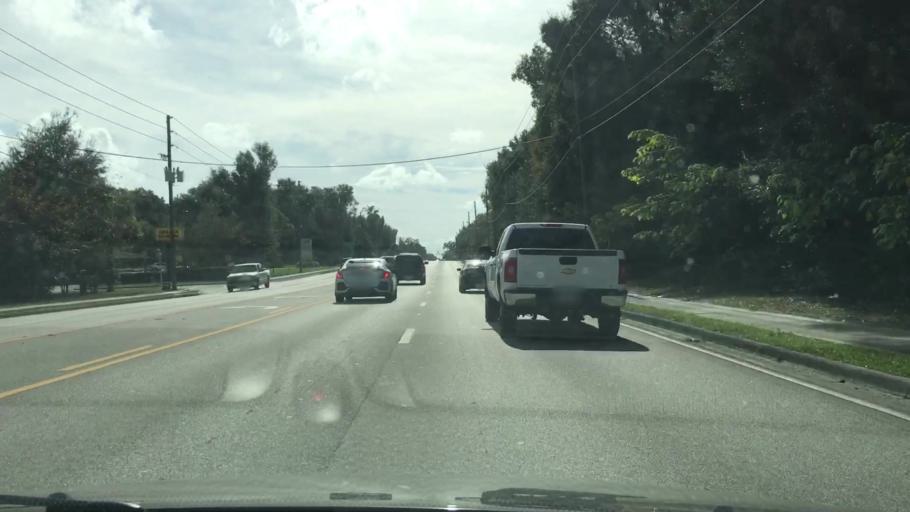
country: US
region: Florida
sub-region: Volusia County
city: DeLand
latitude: 29.0397
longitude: -81.3246
